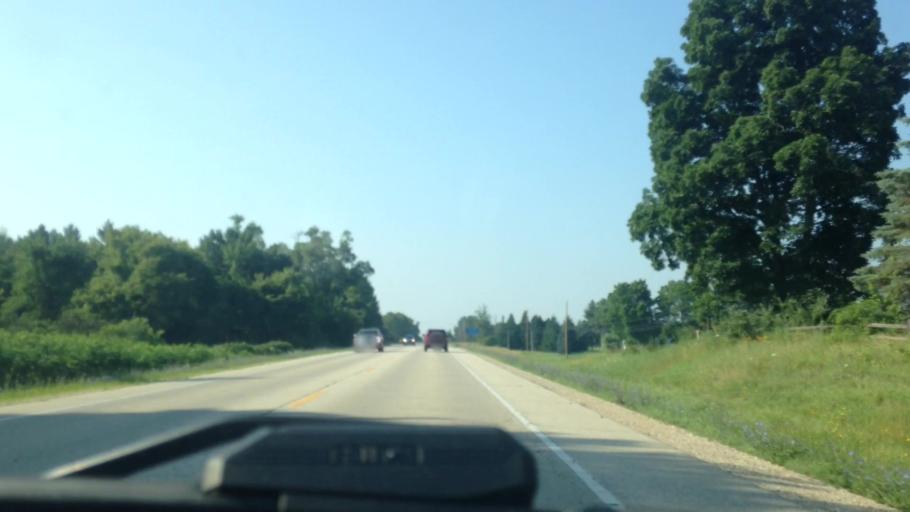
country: US
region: Wisconsin
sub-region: Washington County
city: Slinger
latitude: 43.2924
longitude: -88.2609
